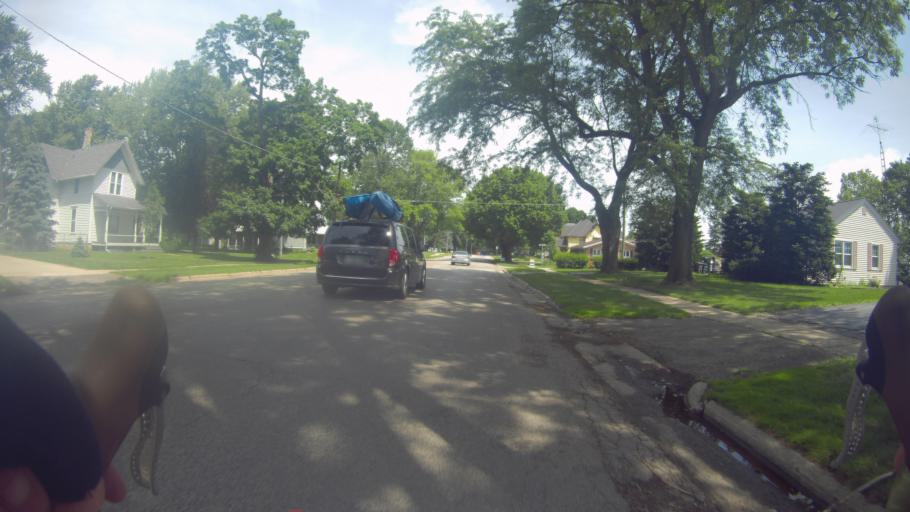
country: US
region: Wisconsin
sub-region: Jefferson County
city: Lake Mills
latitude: 43.0721
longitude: -88.9137
